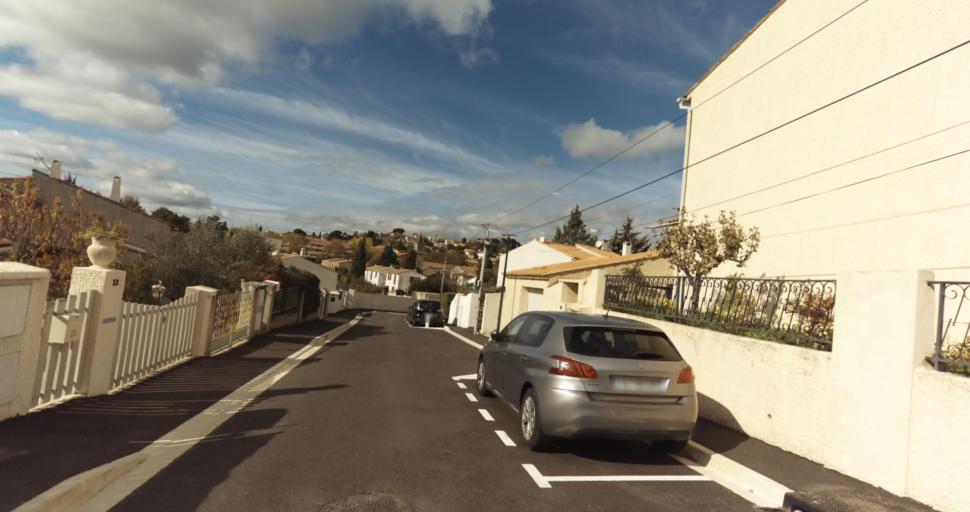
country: FR
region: Provence-Alpes-Cote d'Azur
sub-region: Departement des Bouches-du-Rhone
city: Venelles
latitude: 43.5966
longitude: 5.4874
